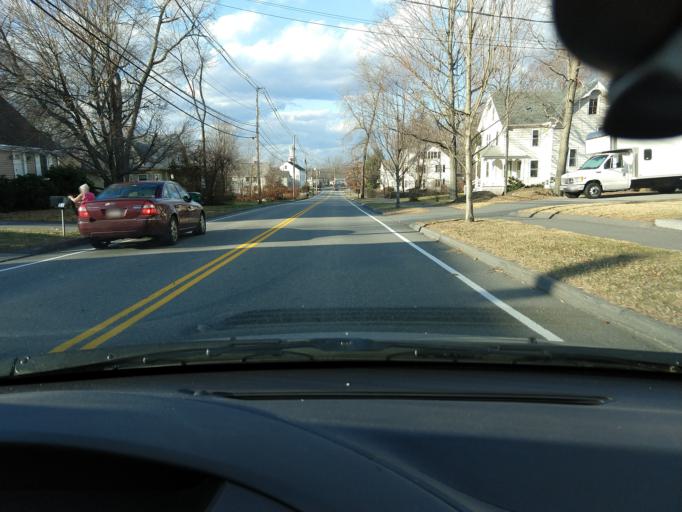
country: US
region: Massachusetts
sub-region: Middlesex County
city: Littleton Common
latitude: 42.5439
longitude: -71.4722
